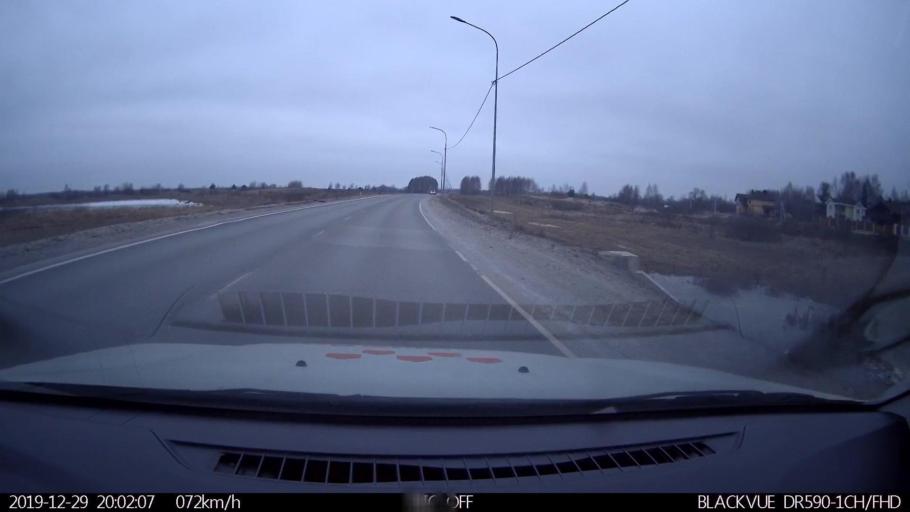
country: RU
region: Nizjnij Novgorod
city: Bor
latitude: 56.3627
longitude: 44.0339
